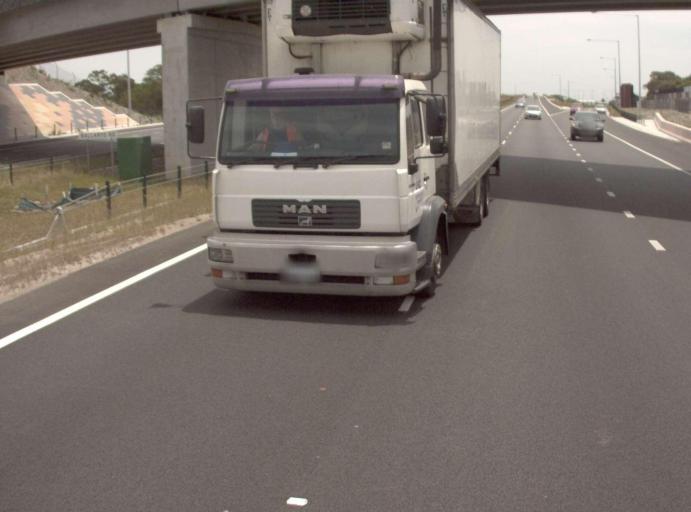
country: AU
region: Victoria
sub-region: Frankston
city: Carrum Downs
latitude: -38.1139
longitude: 145.1649
